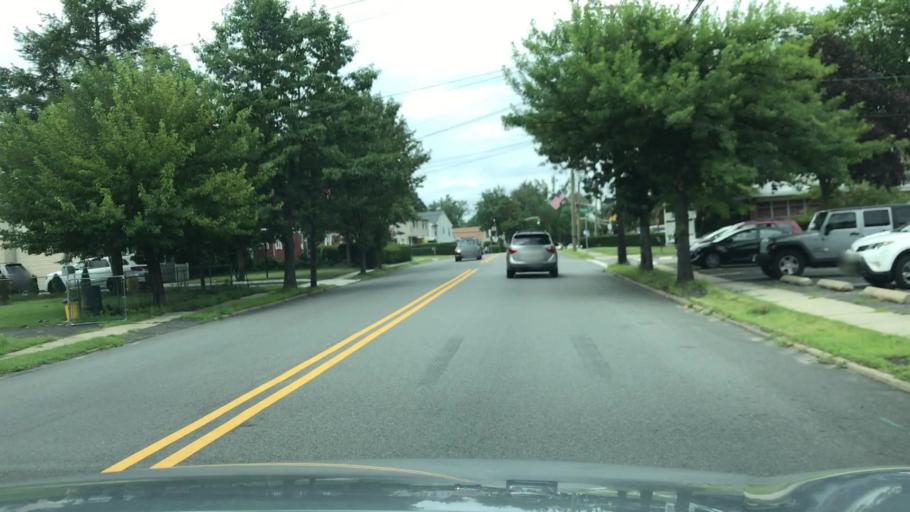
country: US
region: New Jersey
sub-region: Bergen County
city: River Edge
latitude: 40.9199
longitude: -74.0268
